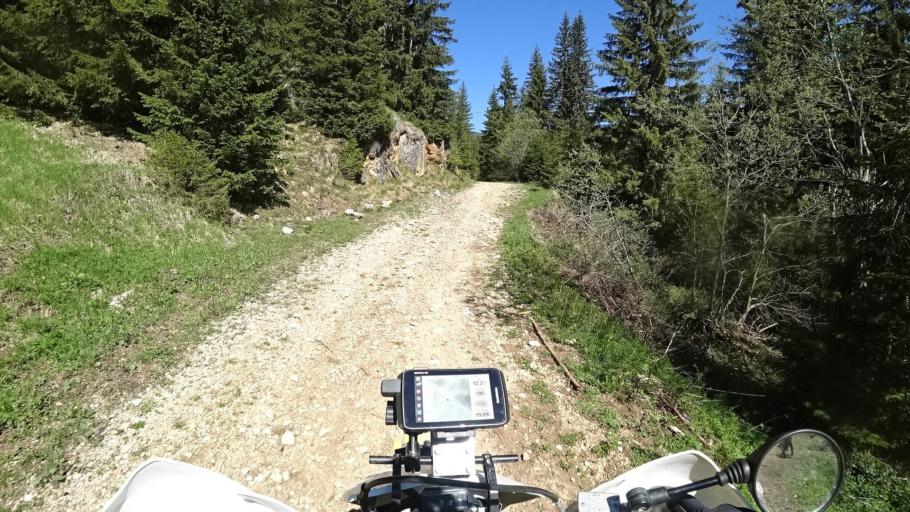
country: BA
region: Federation of Bosnia and Herzegovina
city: Rumboci
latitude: 43.8561
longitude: 17.4972
